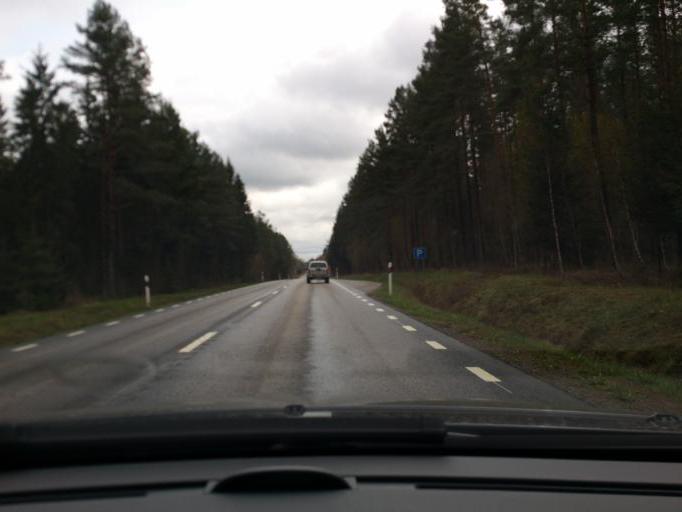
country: SE
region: Kronoberg
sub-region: Vaxjo Kommun
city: Ingelstad
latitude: 56.7946
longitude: 14.8946
